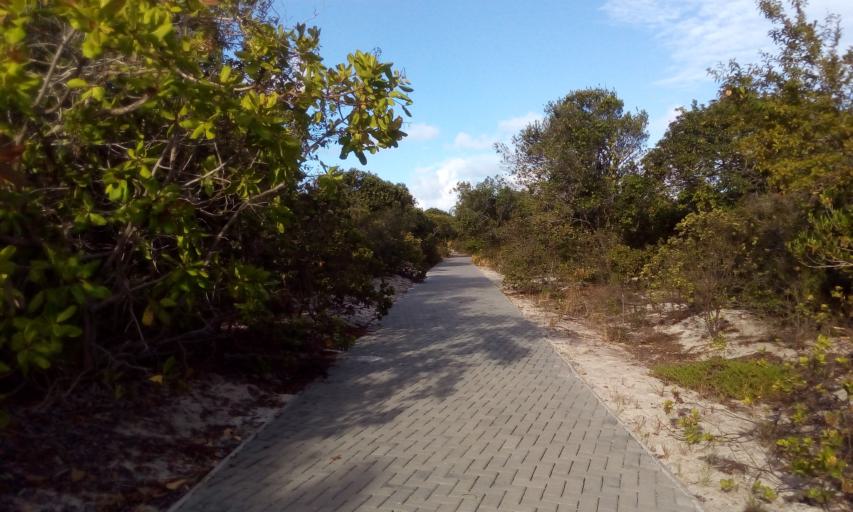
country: BR
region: Bahia
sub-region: Mata De Sao Joao
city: Mata de Sao Joao
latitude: -12.5730
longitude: -38.0083
